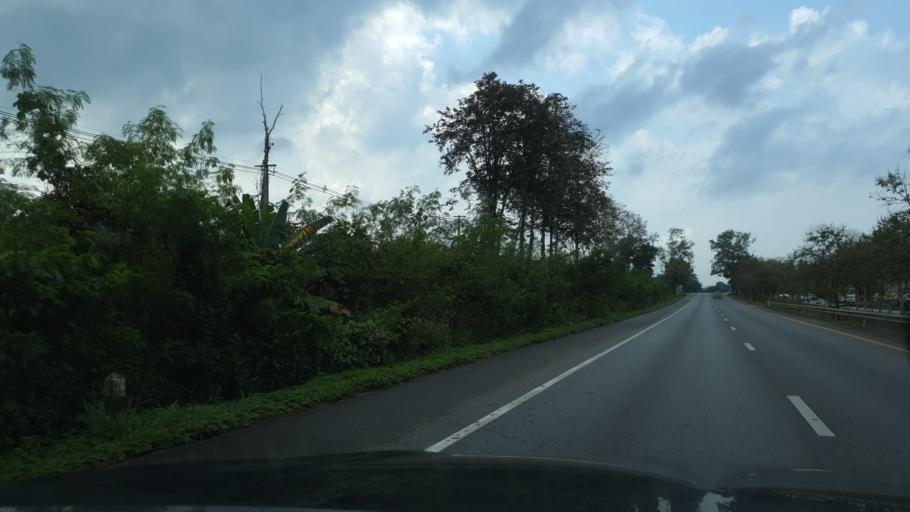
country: TH
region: Chumphon
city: Pathio
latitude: 10.9182
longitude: 99.2837
